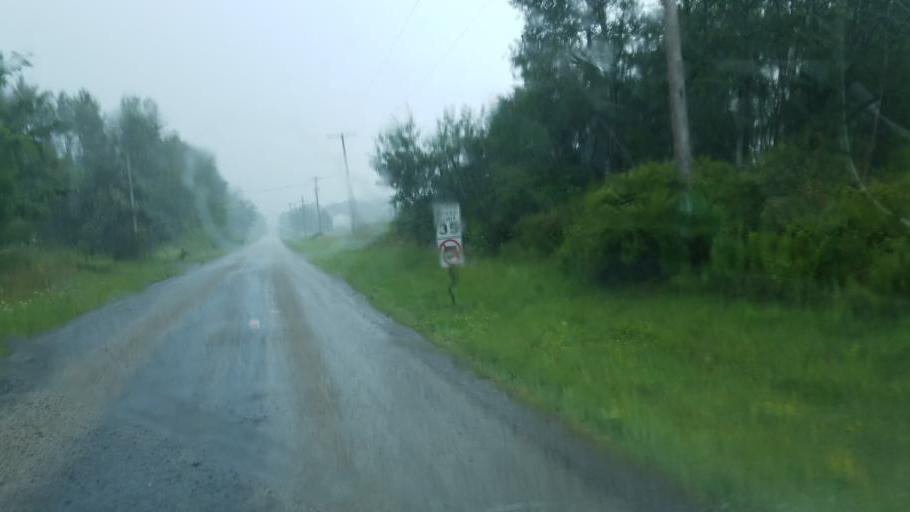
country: US
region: Ohio
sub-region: Ashtabula County
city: Orwell
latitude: 41.5352
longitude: -80.9825
